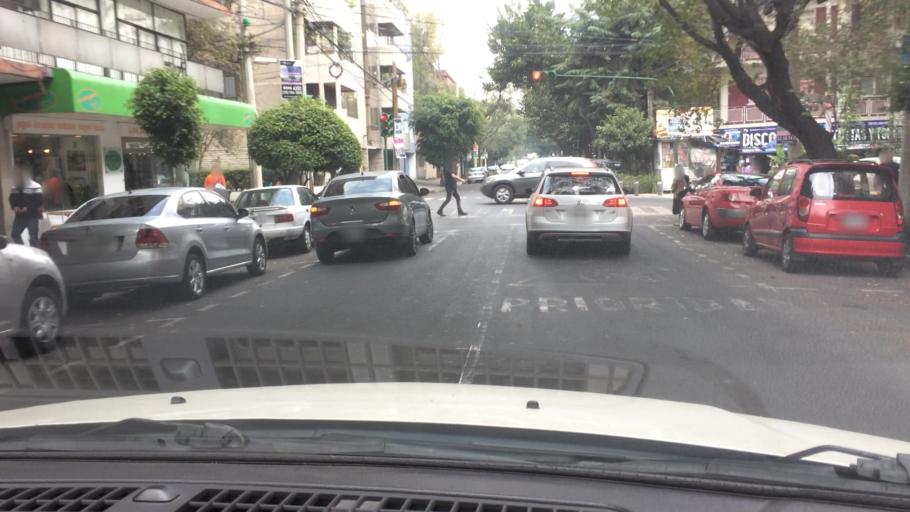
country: MX
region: Mexico City
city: Colonia del Valle
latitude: 19.3964
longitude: -99.1740
